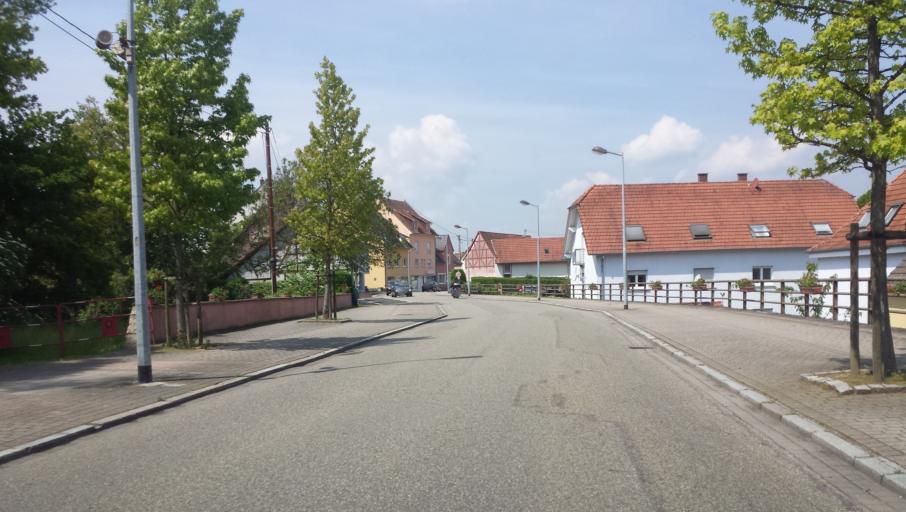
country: DE
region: Rheinland-Pfalz
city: Berg
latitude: 48.9752
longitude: 8.1750
